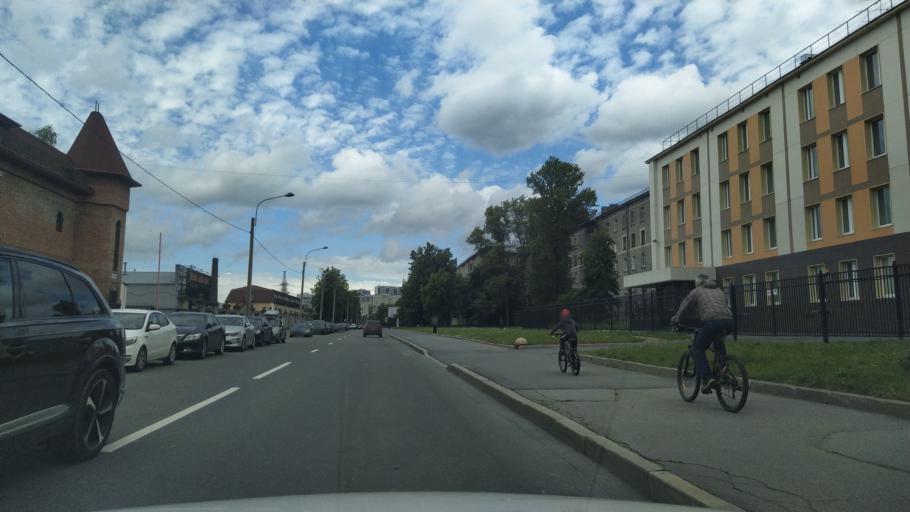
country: RU
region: Leningrad
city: Finlyandskiy
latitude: 59.9727
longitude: 30.3849
